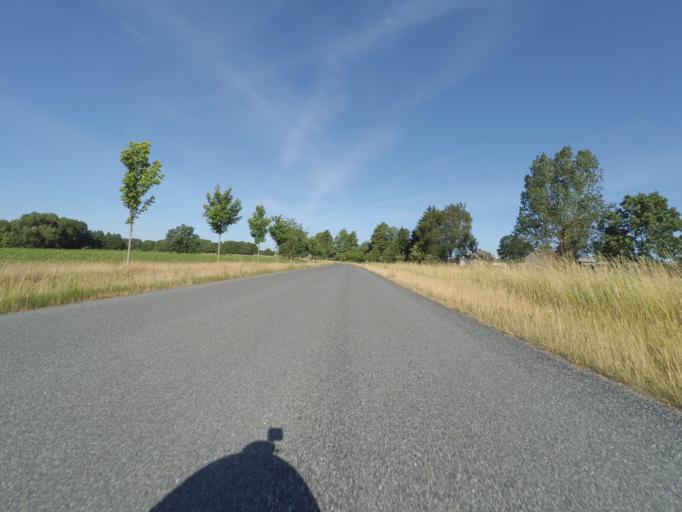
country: DE
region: Mecklenburg-Vorpommern
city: Lubz
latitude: 53.3698
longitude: 12.1141
